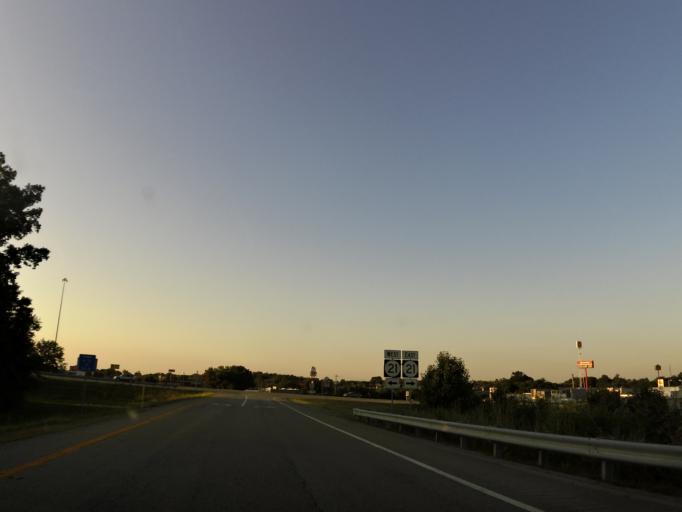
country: US
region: Kentucky
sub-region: Madison County
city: Berea
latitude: 37.5677
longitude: -84.3138
